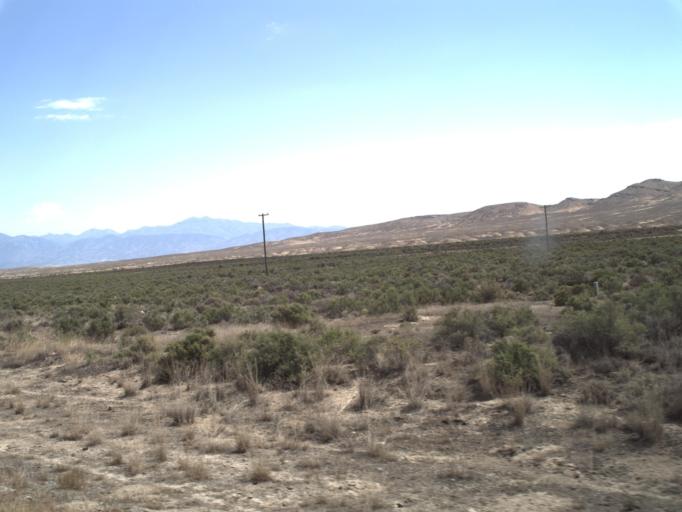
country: US
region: Utah
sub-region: Tooele County
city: Tooele
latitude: 40.1162
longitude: -112.4308
